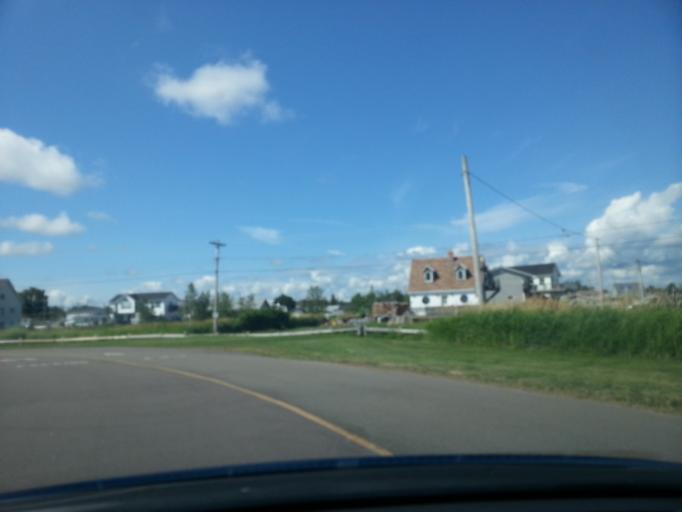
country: CA
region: New Brunswick
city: Shediac
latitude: 46.2389
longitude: -64.5117
